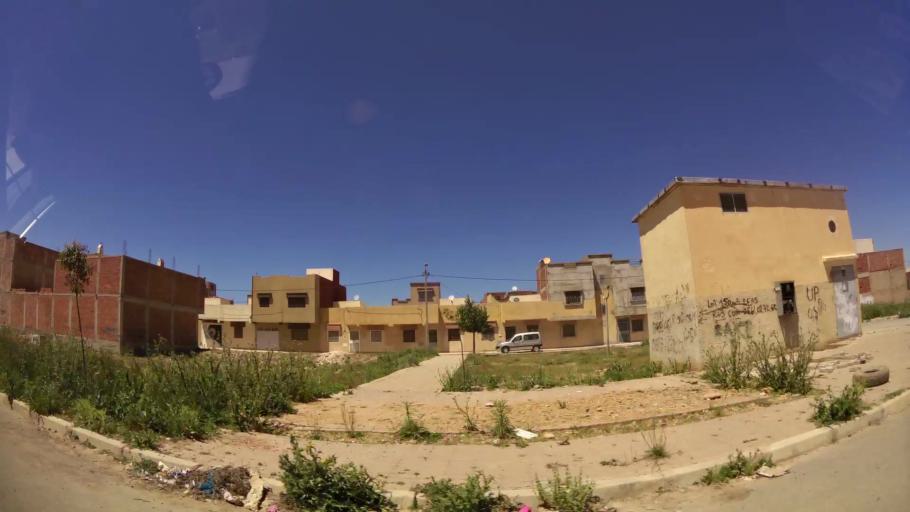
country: MA
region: Oriental
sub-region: Oujda-Angad
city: Oujda
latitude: 34.6815
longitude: -1.8550
